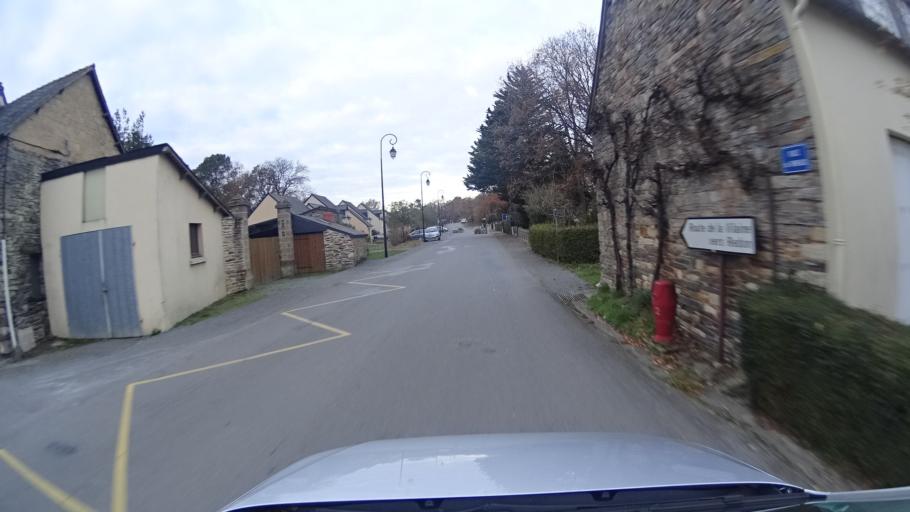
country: FR
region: Brittany
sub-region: Departement d'Ille-et-Vilaine
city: Langon
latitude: 47.6982
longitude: -1.8956
